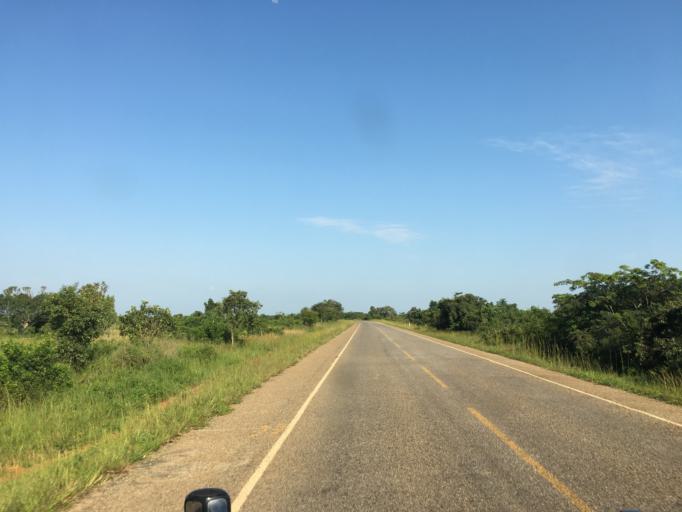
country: UG
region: Western Region
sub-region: Kiryandongo District
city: Masindi Port
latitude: 1.5751
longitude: 31.9416
